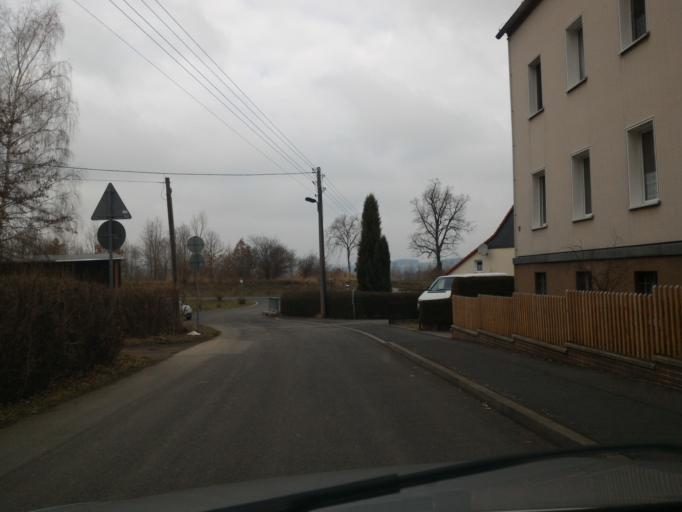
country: DE
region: Saxony
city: Olbersdorf
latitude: 50.8852
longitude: 14.7853
